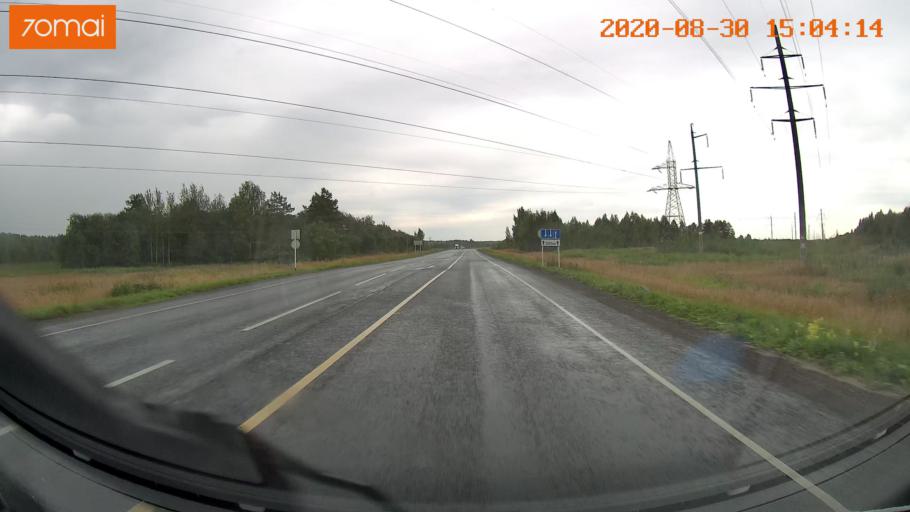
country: RU
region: Ivanovo
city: Staraya Vichuga
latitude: 57.2893
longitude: 41.9081
